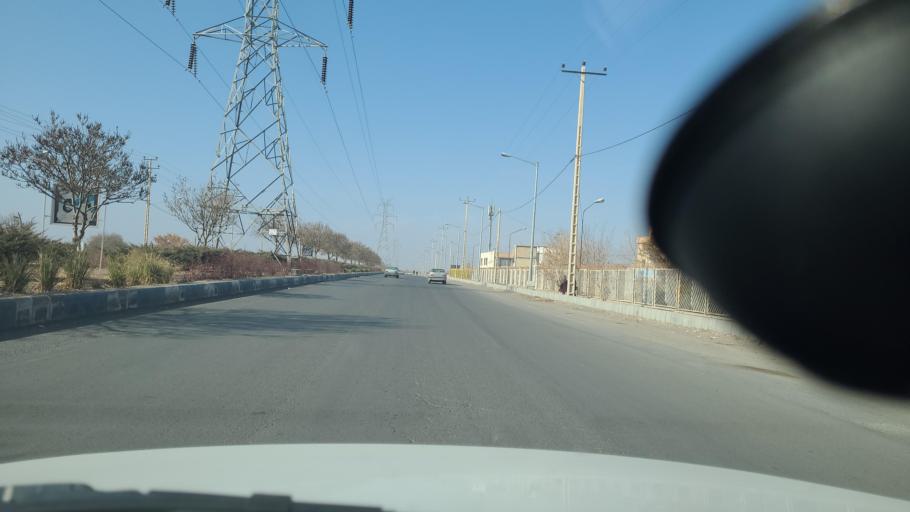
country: IR
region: Razavi Khorasan
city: Fariman
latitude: 35.6951
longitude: 59.8436
